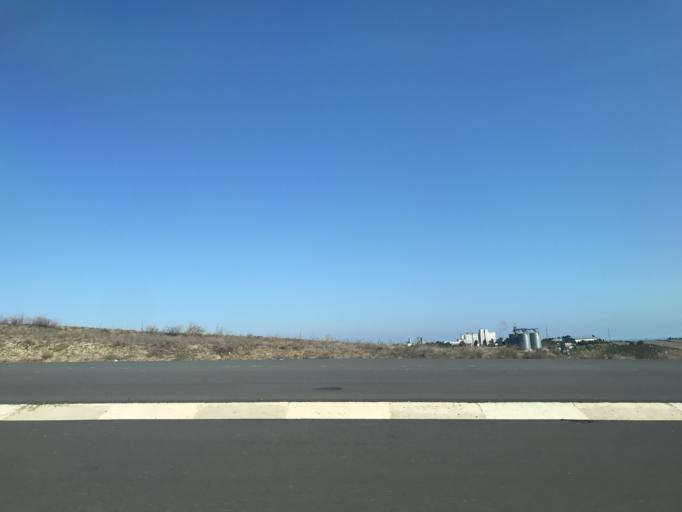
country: TR
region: Tekirdag
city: Kumbag
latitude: 40.9422
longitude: 27.4344
